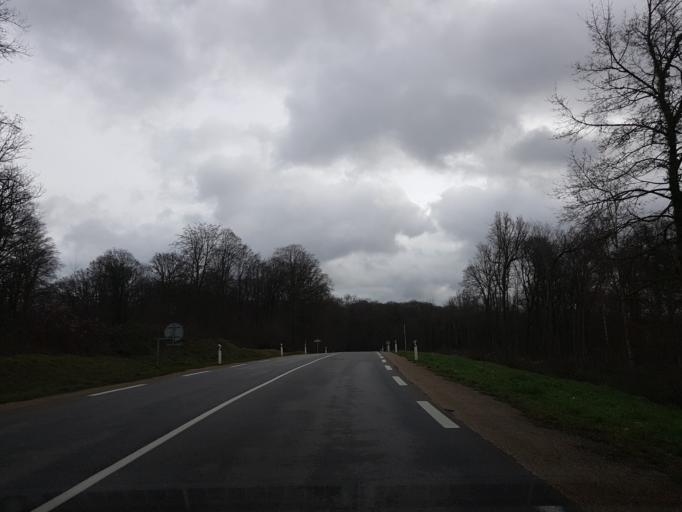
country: FR
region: Champagne-Ardenne
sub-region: Departement de la Haute-Marne
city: Fayl-Billot
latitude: 47.8068
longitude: 5.5567
